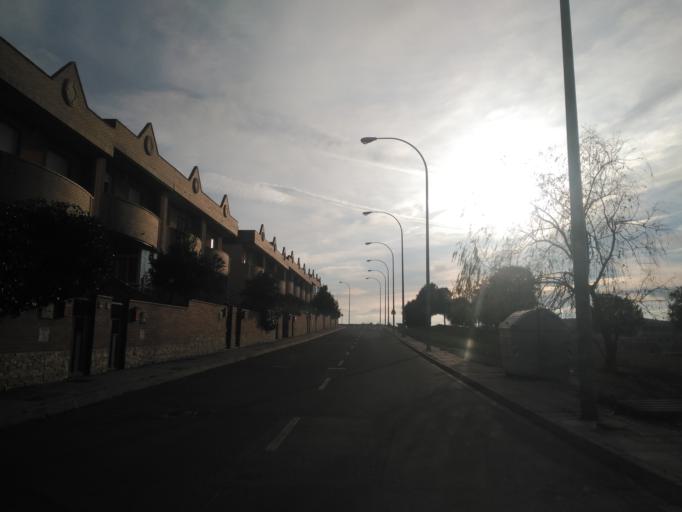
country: ES
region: Castille and Leon
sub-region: Provincia de Salamanca
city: Salamanca
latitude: 40.9481
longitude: -5.6731
